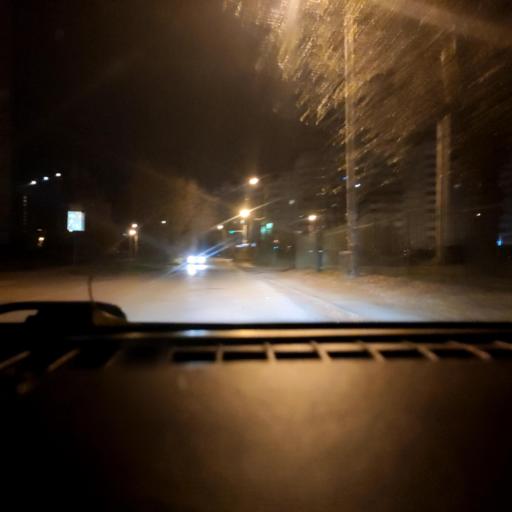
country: RU
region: Perm
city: Perm
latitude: 57.9707
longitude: 56.2265
